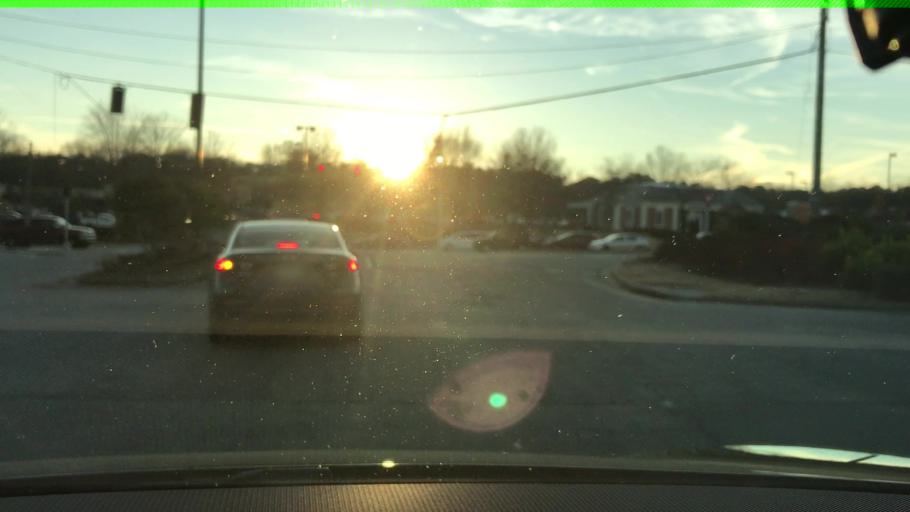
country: US
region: Georgia
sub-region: Fulton County
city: Johns Creek
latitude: 34.0147
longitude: -84.1848
